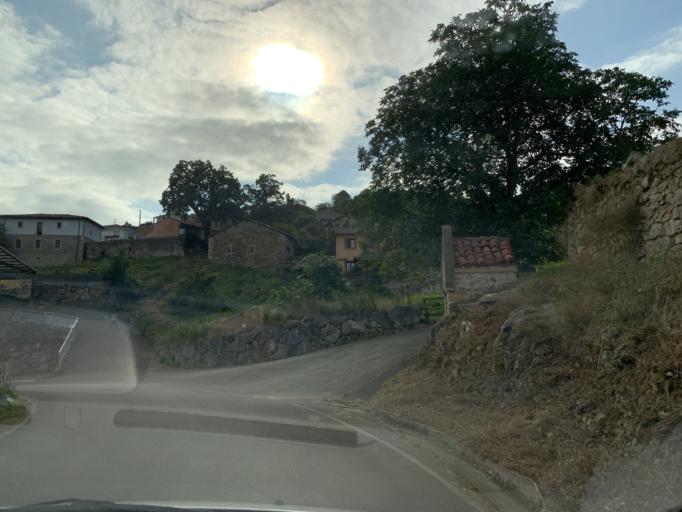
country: ES
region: Asturias
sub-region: Province of Asturias
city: Carrena
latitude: 43.3256
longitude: -4.8617
